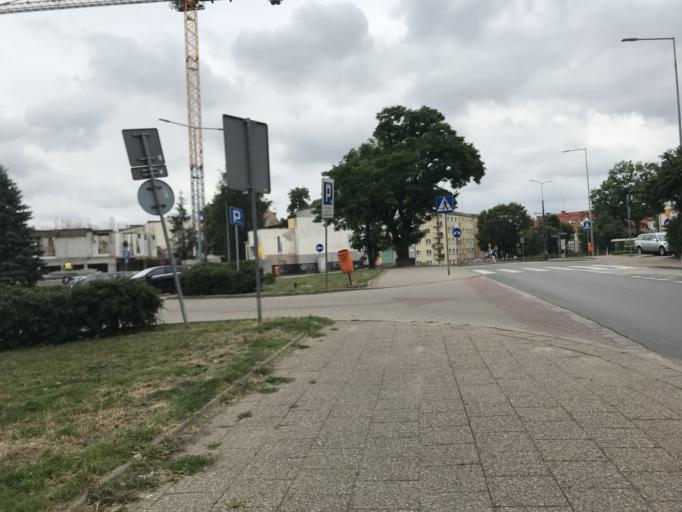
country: PL
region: Warmian-Masurian Voivodeship
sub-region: Powiat elblaski
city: Elblag
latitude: 54.1631
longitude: 19.4061
